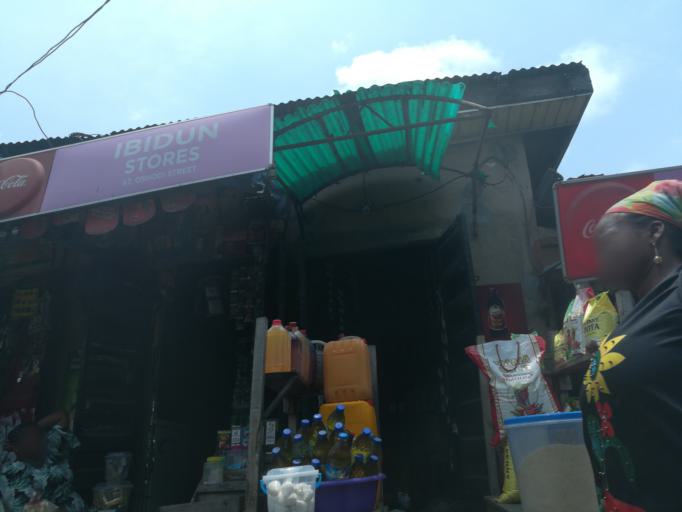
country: NG
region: Lagos
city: Lagos
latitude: 6.4557
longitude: 3.3983
